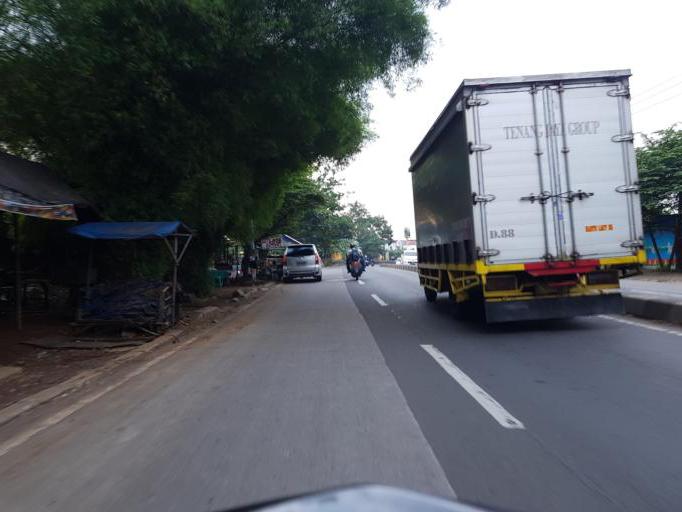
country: ID
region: West Java
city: Parung
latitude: -6.4899
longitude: 106.7379
